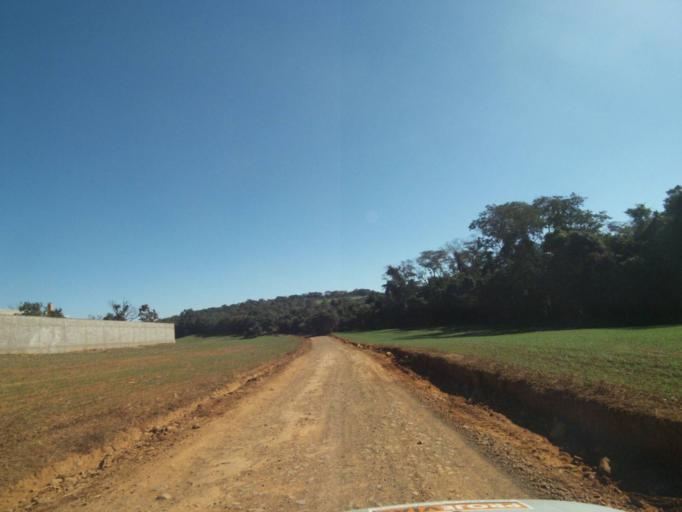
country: BR
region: Parana
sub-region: Tibagi
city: Tibagi
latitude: -24.5797
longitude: -50.6145
